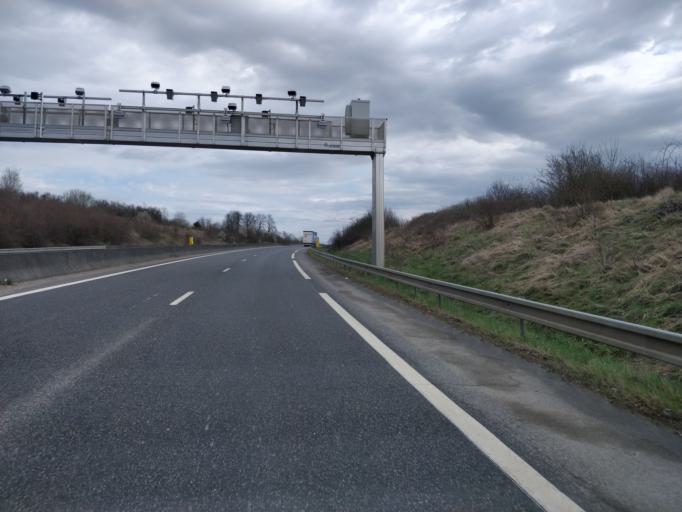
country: FR
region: Lorraine
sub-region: Departement de la Moselle
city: Vitry-sur-Orne
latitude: 49.2726
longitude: 6.1127
